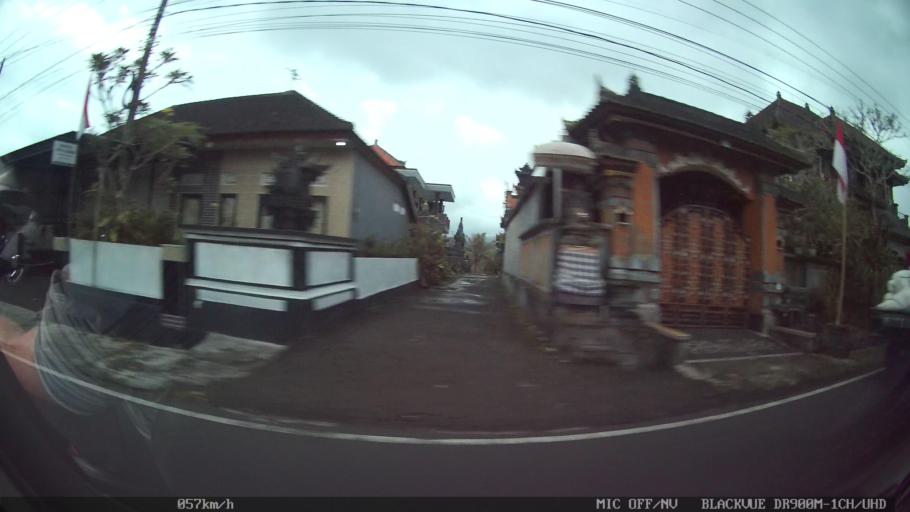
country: ID
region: Bali
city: Empalan
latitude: -8.4015
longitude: 115.1477
